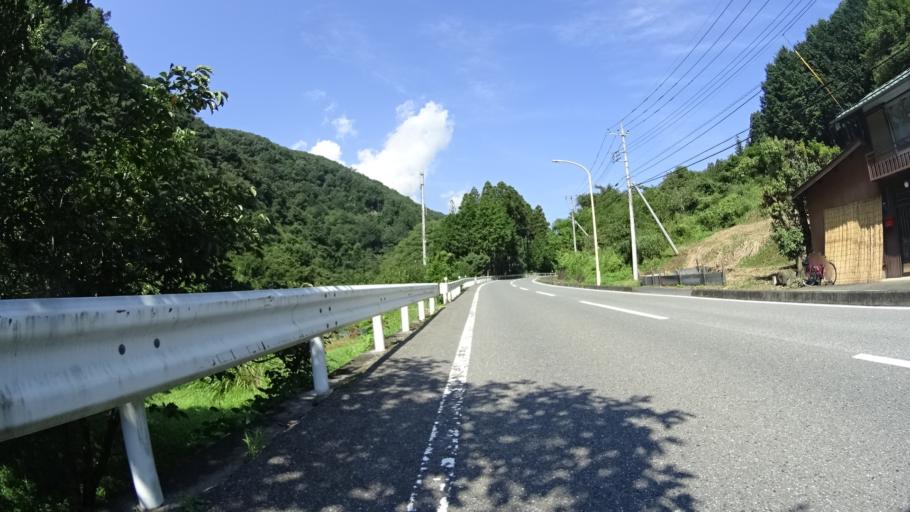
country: JP
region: Saitama
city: Chichibu
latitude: 36.0354
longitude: 138.9201
